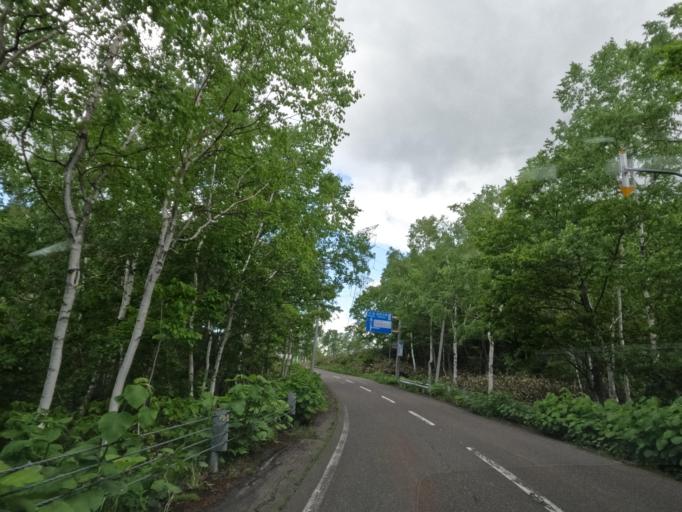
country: JP
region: Hokkaido
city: Tobetsu
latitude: 43.4652
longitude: 141.5996
